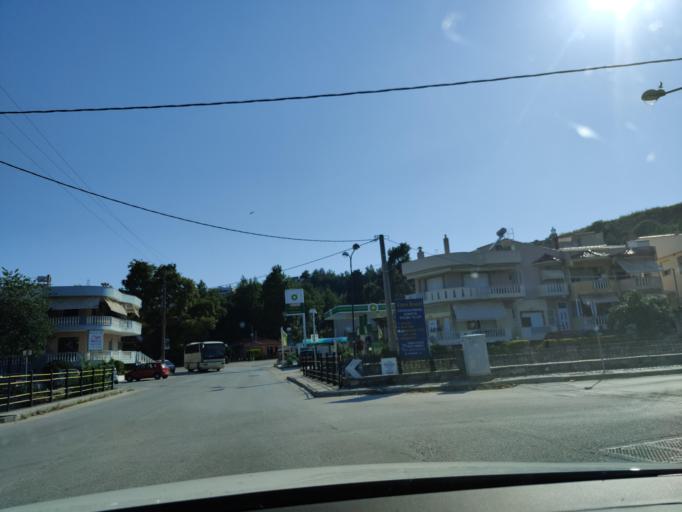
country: GR
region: East Macedonia and Thrace
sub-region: Nomos Kavalas
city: Nea Peramos
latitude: 40.8461
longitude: 24.3068
